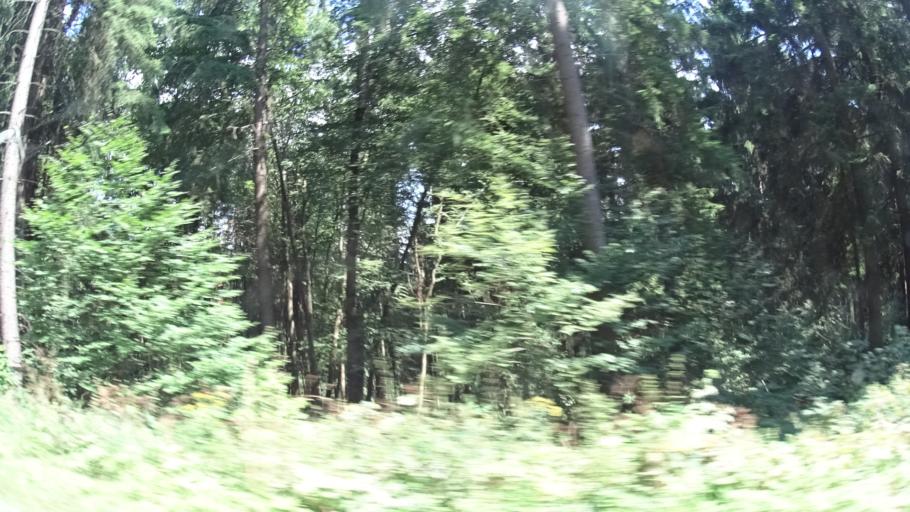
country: DE
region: Thuringia
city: Neustadt am Rennsteig
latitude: 50.5622
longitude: 10.9379
